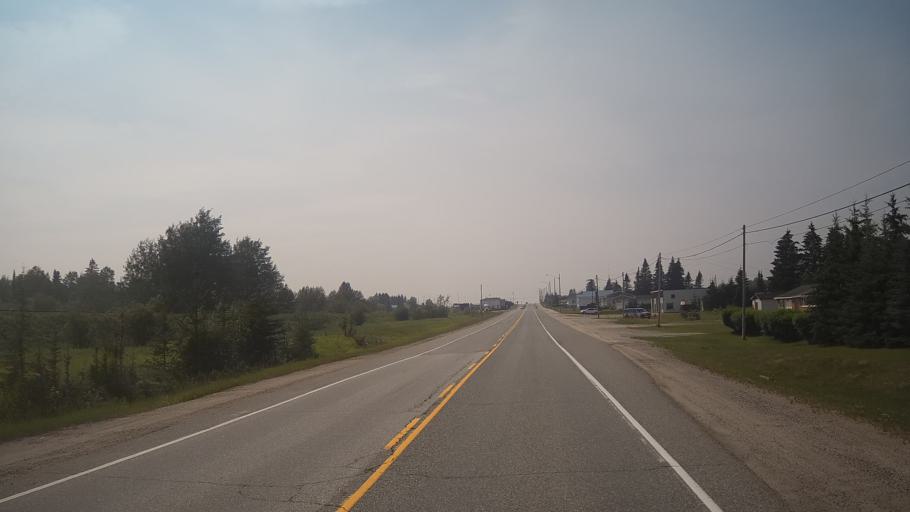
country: CA
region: Ontario
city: Kapuskasing
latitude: 49.3100
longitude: -82.0262
